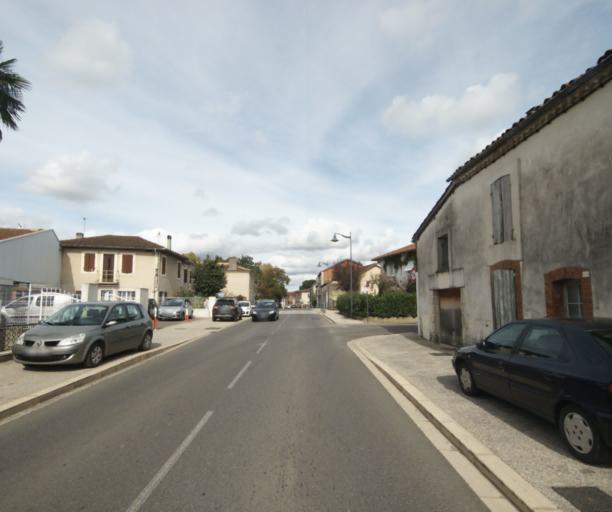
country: FR
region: Midi-Pyrenees
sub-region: Departement du Gers
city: Eauze
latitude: 43.8566
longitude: 0.0995
